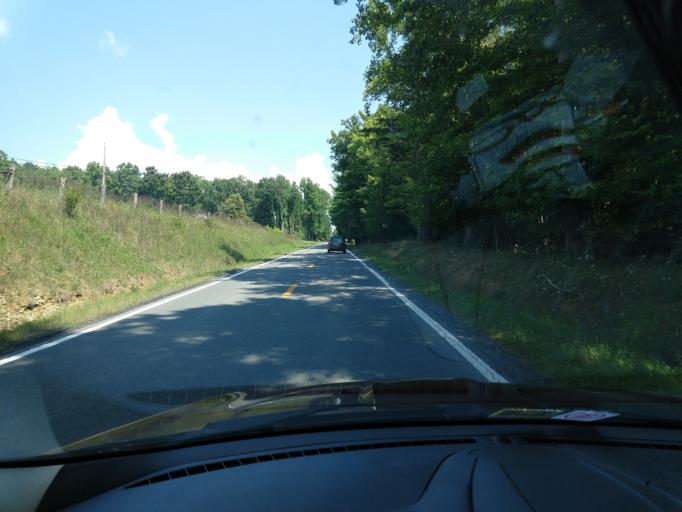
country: US
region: West Virginia
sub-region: Greenbrier County
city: Fairlea
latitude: 37.8310
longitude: -80.5571
